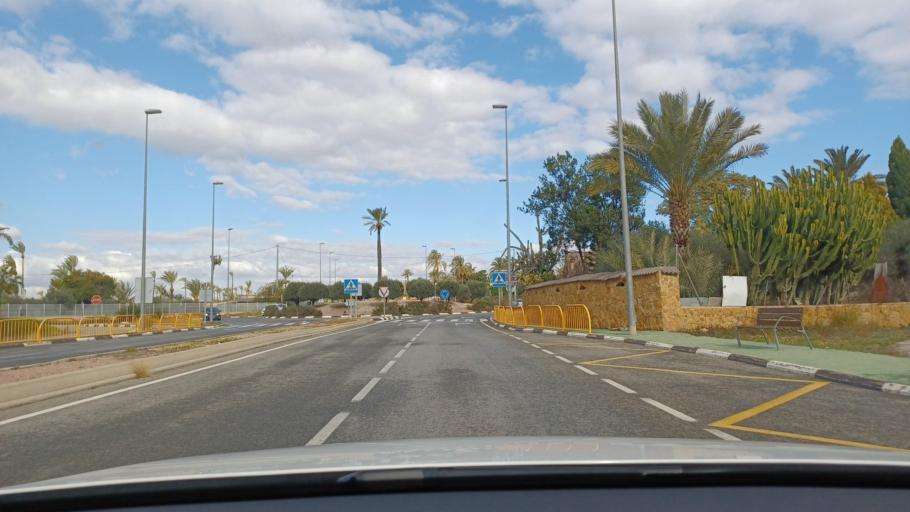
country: ES
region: Valencia
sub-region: Provincia de Alicante
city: Elche
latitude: 38.2391
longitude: -0.7002
